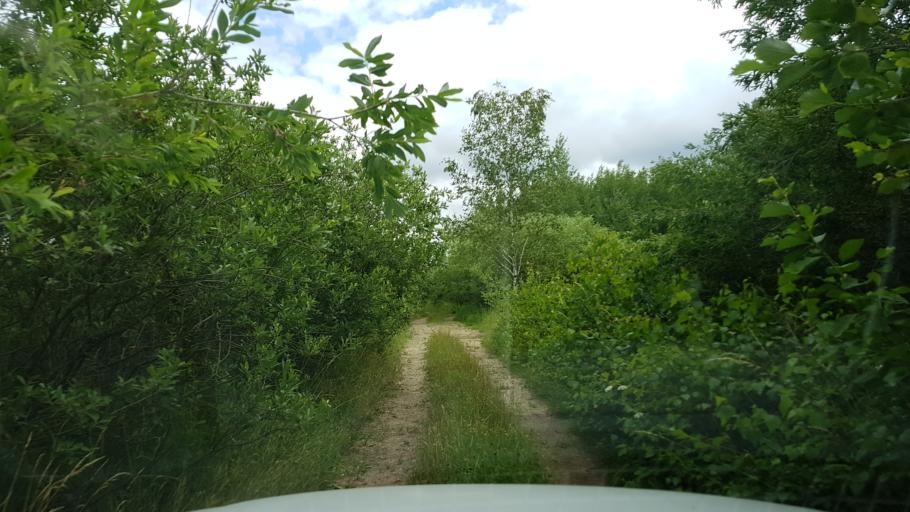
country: PL
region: West Pomeranian Voivodeship
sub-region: Powiat pyrzycki
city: Lipiany
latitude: 52.9470
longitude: 14.9410
